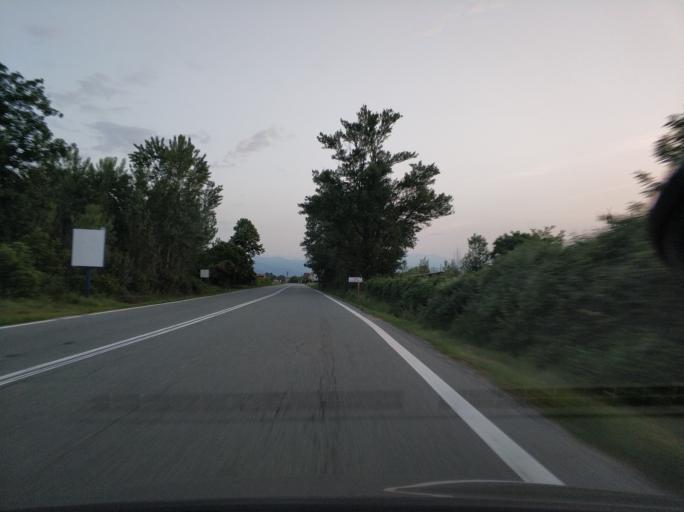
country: IT
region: Piedmont
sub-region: Provincia di Torino
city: Caselle Torinese
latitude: 45.1948
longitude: 7.6407
